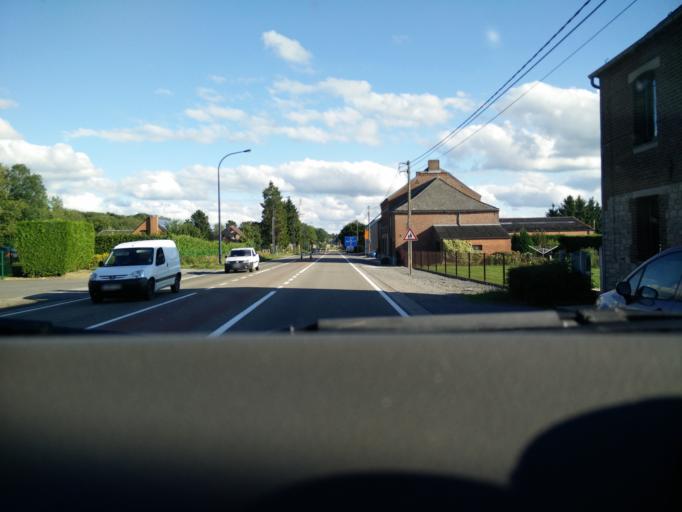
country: BE
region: Wallonia
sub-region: Province du Hainaut
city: Beaumont
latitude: 50.1809
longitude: 4.2243
